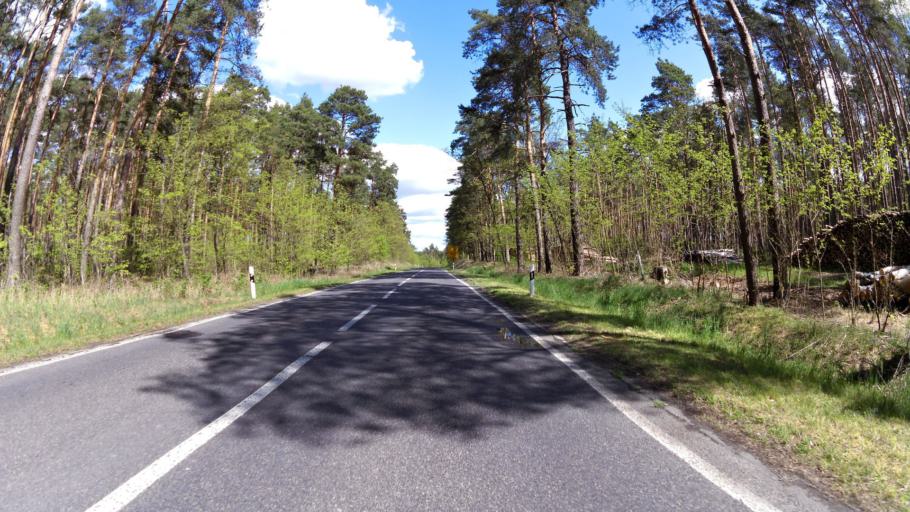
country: DE
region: Brandenburg
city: Wendisch Rietz
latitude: 52.1495
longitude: 13.9744
